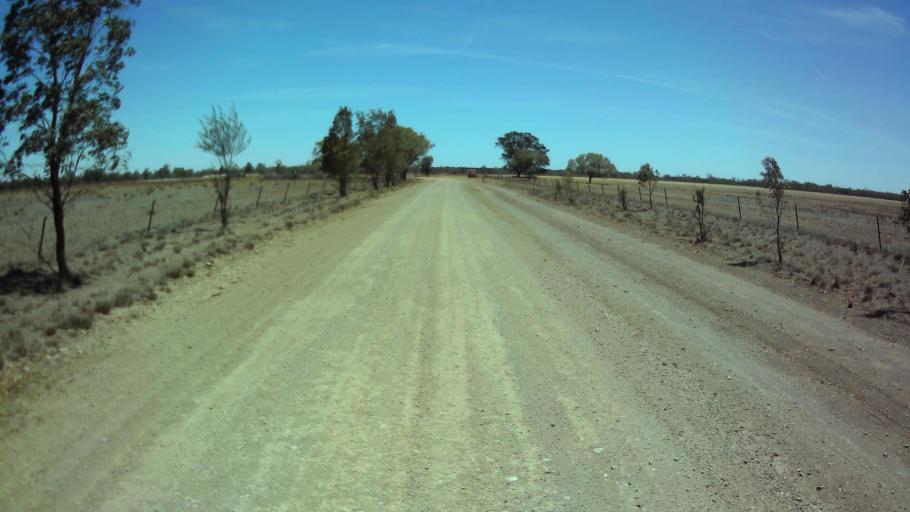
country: AU
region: New South Wales
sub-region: Bland
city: West Wyalong
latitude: -33.8221
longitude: 147.6436
